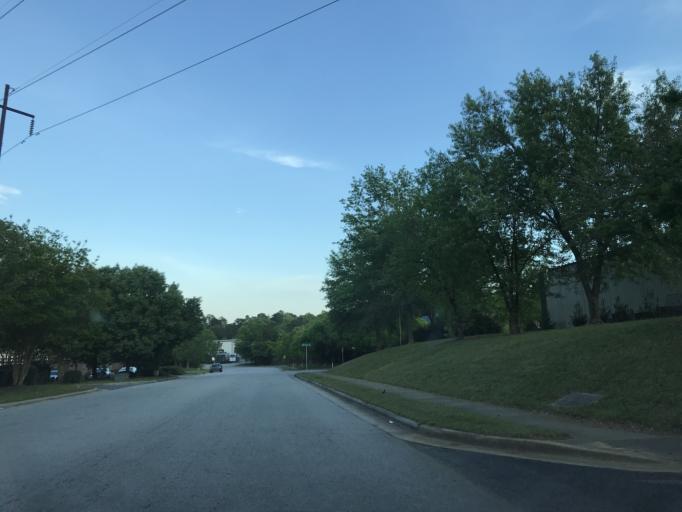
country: US
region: North Carolina
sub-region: Wake County
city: Knightdale
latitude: 35.7667
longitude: -78.5530
